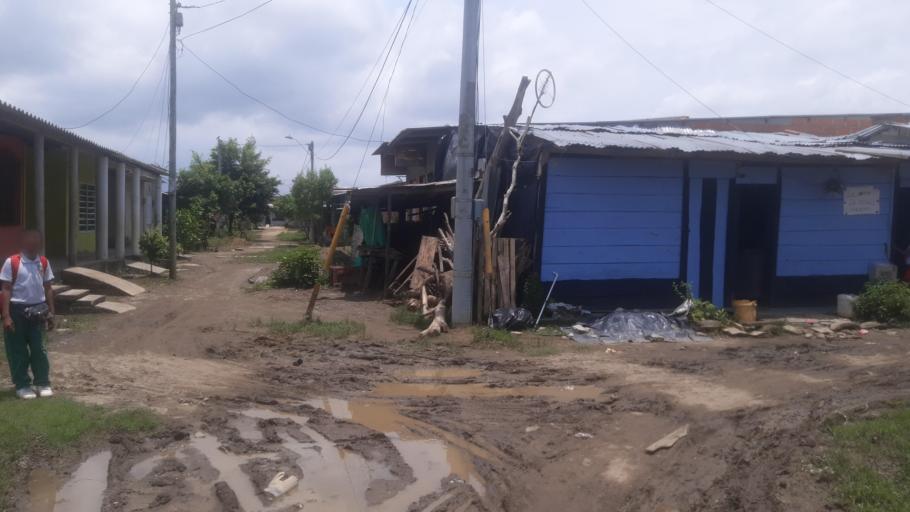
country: CO
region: Antioquia
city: Apartado
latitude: 8.0011
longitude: -76.6289
